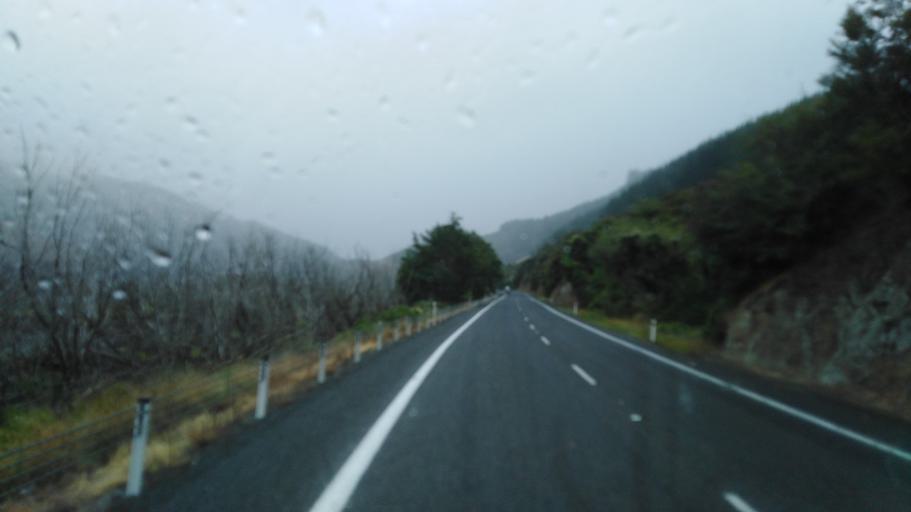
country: NZ
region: Marlborough
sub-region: Marlborough District
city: Blenheim
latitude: -41.4044
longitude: 173.9579
